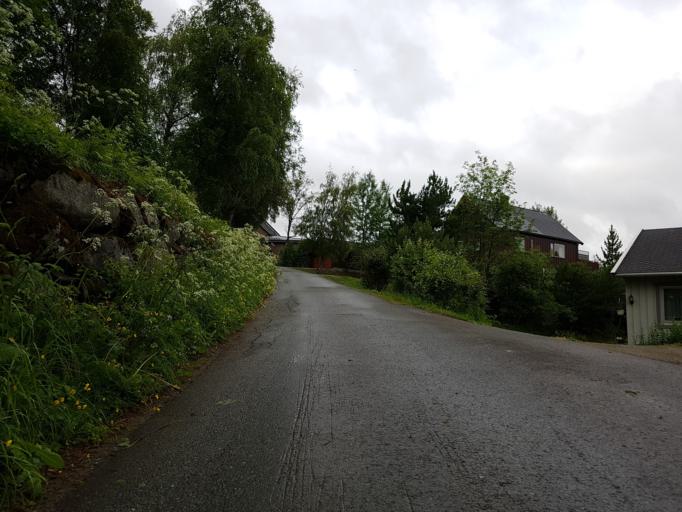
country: NO
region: Sor-Trondelag
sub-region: Selbu
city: Mebonden
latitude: 63.2296
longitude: 11.0335
